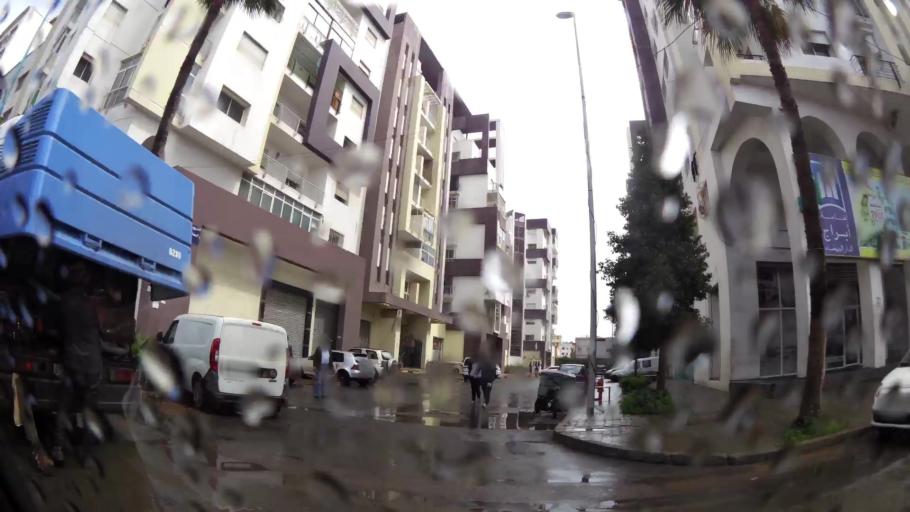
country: MA
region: Grand Casablanca
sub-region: Casablanca
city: Casablanca
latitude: 33.5706
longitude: -7.5964
